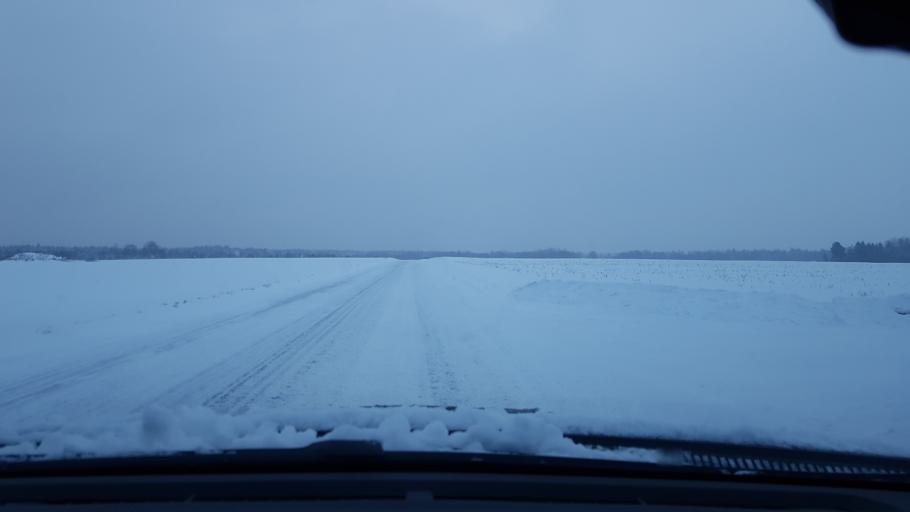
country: EE
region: Harju
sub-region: Anija vald
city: Kehra
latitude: 59.3853
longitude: 25.3149
